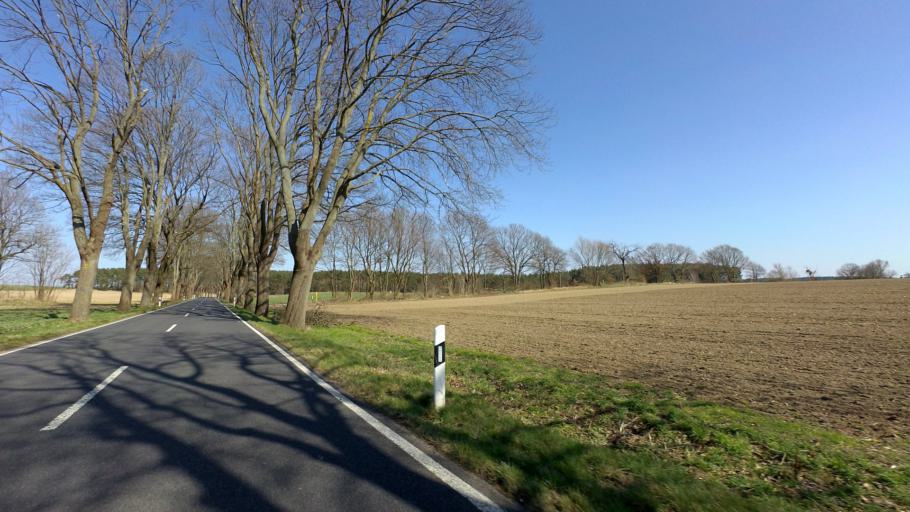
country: DE
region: Brandenburg
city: Sonnenberg
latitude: 52.9936
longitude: 13.0616
